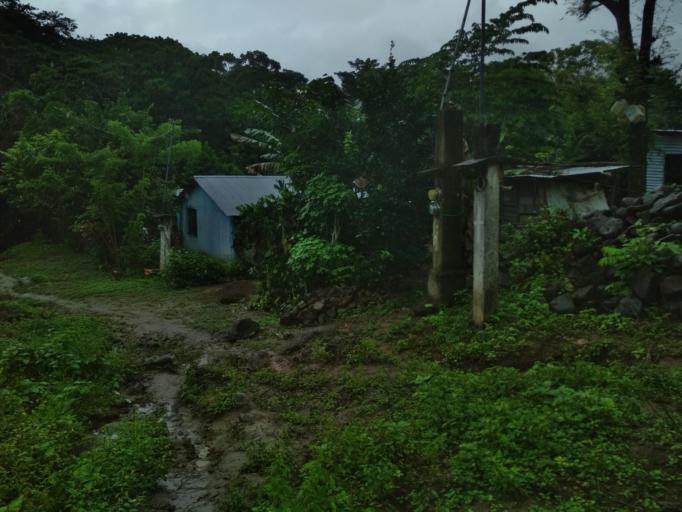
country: MX
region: Veracruz
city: Santiago Tuxtla
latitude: 18.4186
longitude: -95.3050
